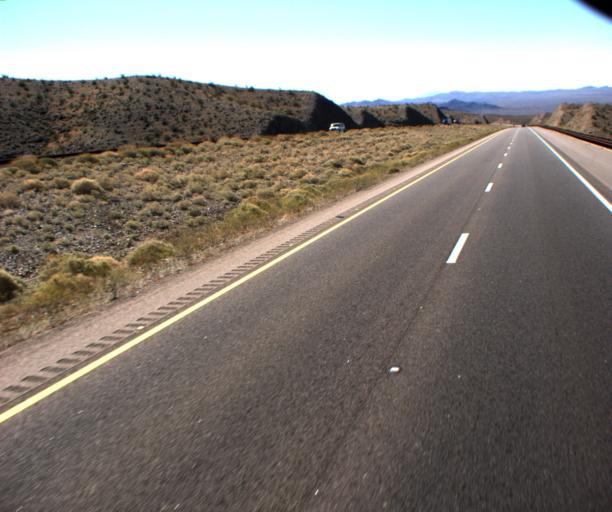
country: US
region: Nevada
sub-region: Clark County
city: Boulder City
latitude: 35.9056
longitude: -114.6278
